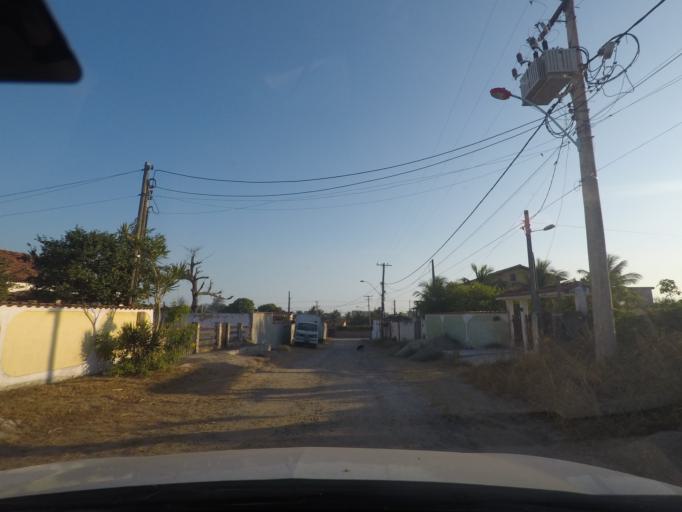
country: BR
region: Rio de Janeiro
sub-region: Marica
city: Marica
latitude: -22.9699
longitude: -42.9298
